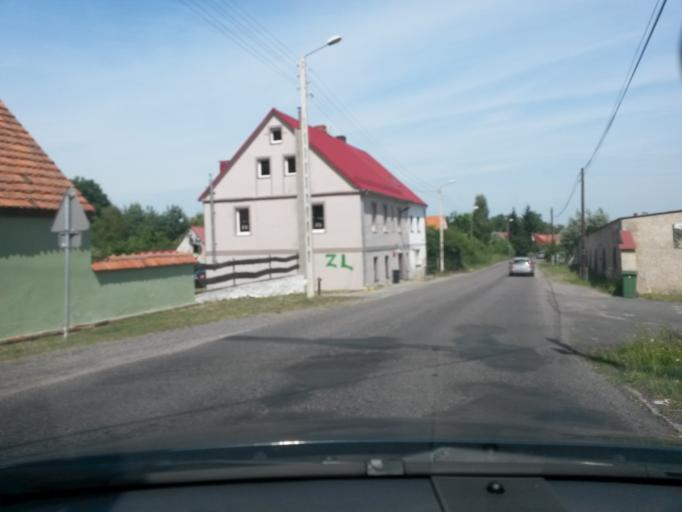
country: PL
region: Lower Silesian Voivodeship
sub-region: Powiat legnicki
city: Prochowice
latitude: 51.2422
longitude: 16.3637
